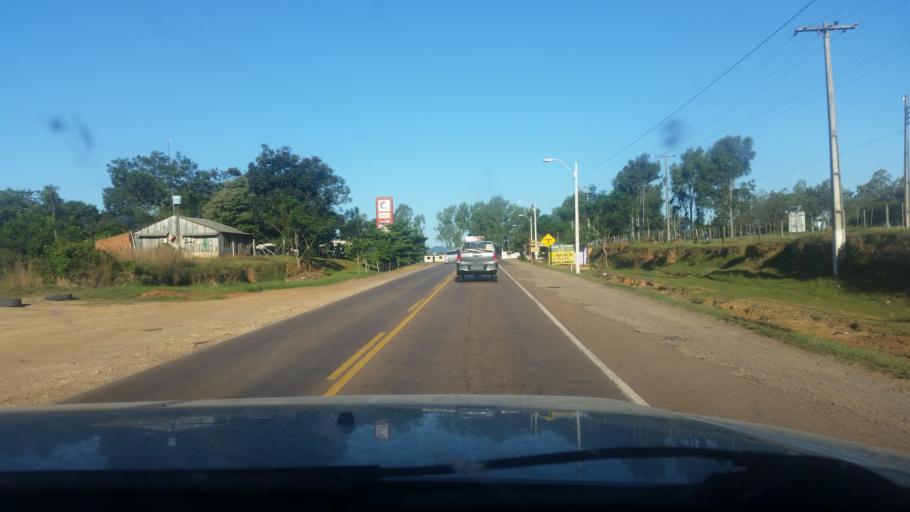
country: PY
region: Guaira
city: Villarrica
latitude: -25.7538
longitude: -56.4378
